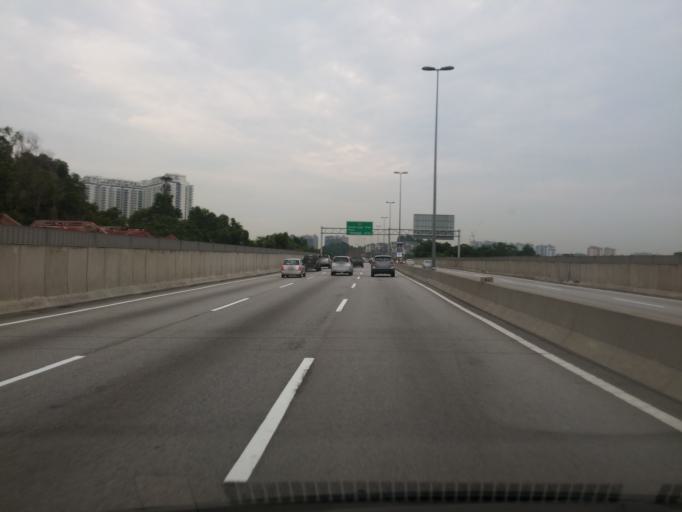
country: MY
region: Kuala Lumpur
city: Kuala Lumpur
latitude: 3.0726
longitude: 101.6876
